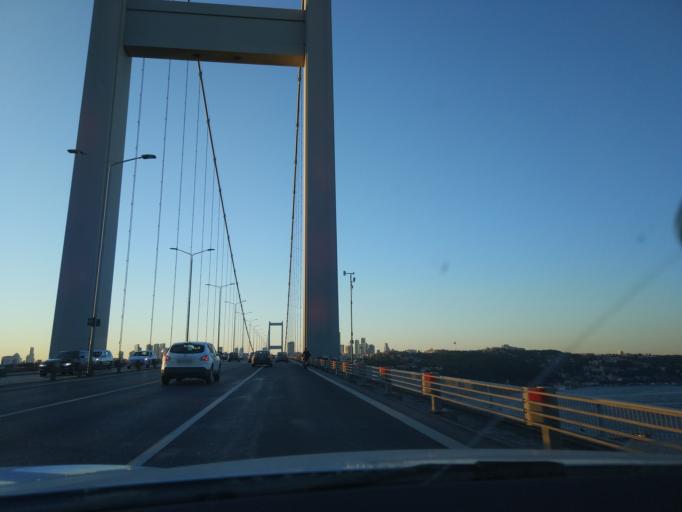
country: TR
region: Istanbul
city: UEskuedar
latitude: 41.0414
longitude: 29.0388
